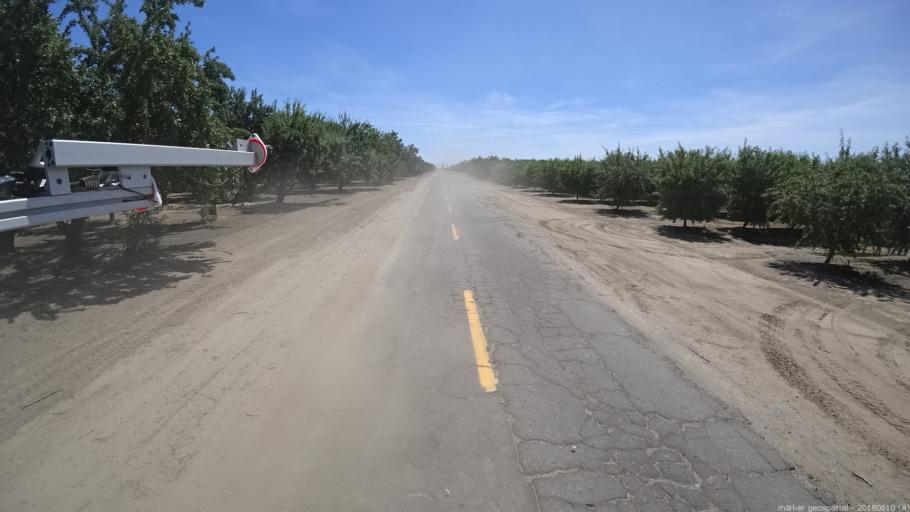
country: US
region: California
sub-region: Madera County
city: Chowchilla
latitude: 37.0399
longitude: -120.3891
